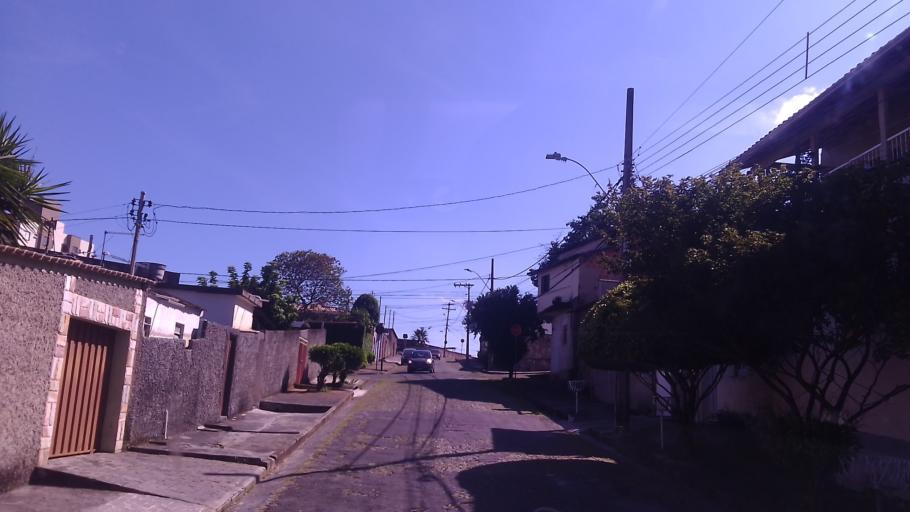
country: BR
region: Minas Gerais
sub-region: Contagem
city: Contagem
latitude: -19.9032
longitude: -44.0164
